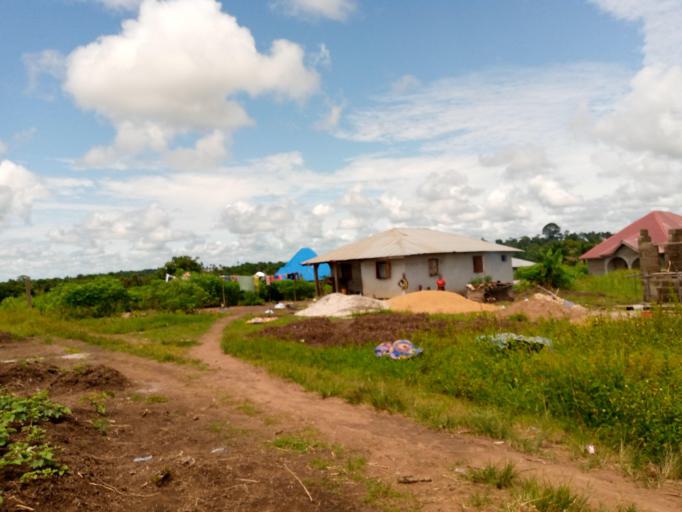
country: SL
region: Northern Province
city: Magburaka
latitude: 8.7173
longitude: -11.9253
